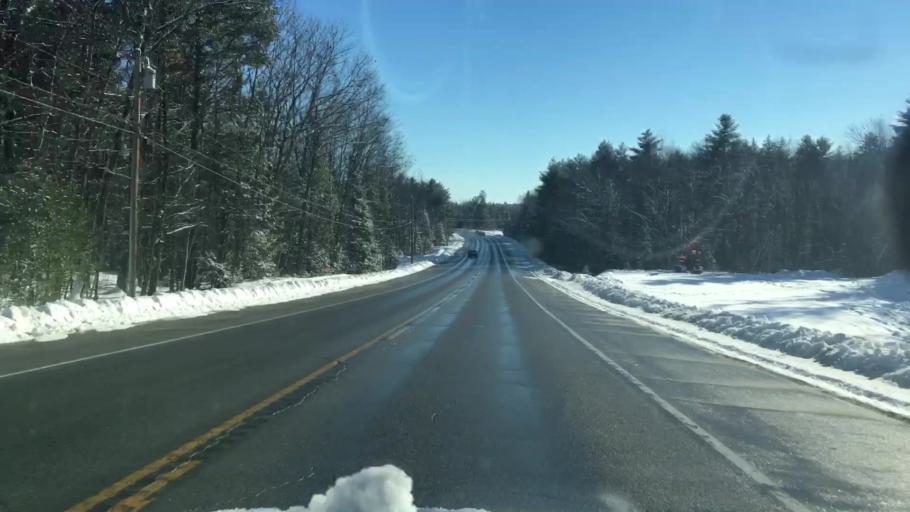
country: US
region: Maine
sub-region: Cumberland County
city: Bridgton
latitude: 44.0126
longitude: -70.6796
